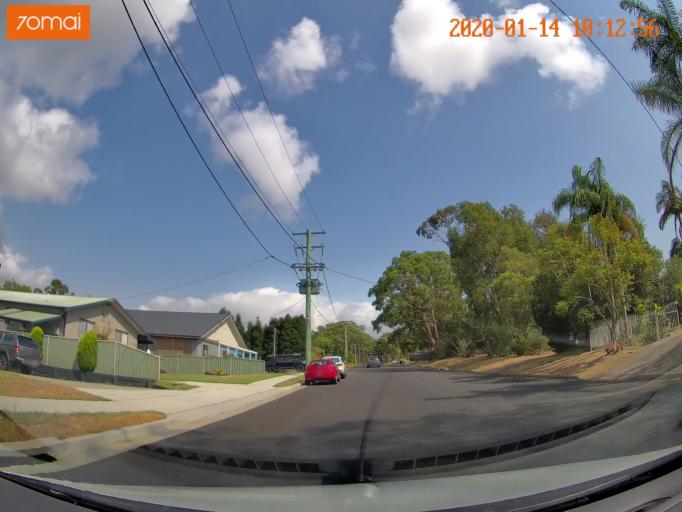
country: AU
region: New South Wales
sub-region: Lake Macquarie Shire
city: Dora Creek
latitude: -33.1144
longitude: 151.5297
